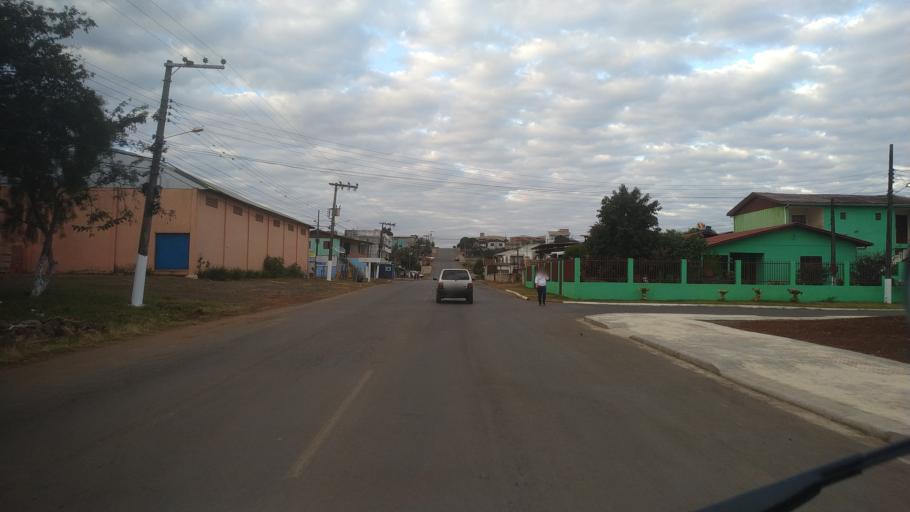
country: BR
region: Santa Catarina
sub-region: Chapeco
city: Chapeco
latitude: -27.1018
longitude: -52.6799
